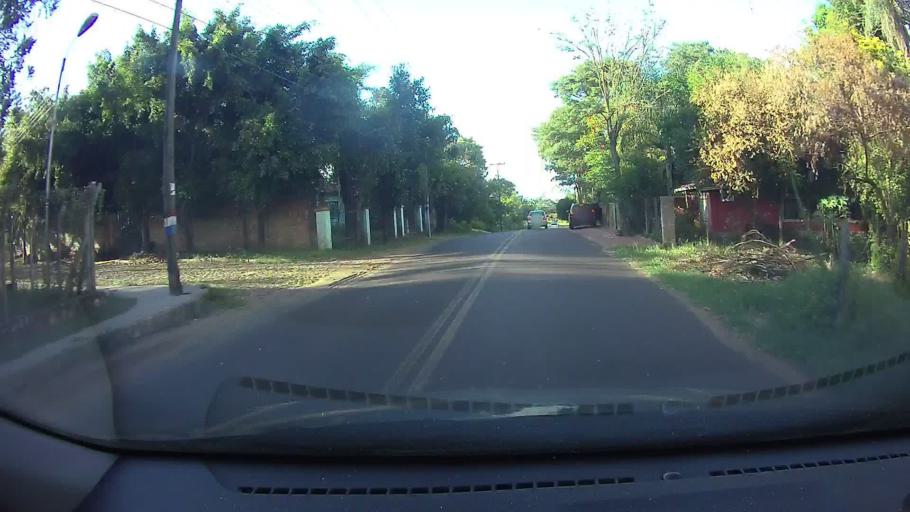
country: PY
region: Cordillera
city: Altos
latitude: -25.1747
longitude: -57.2310
